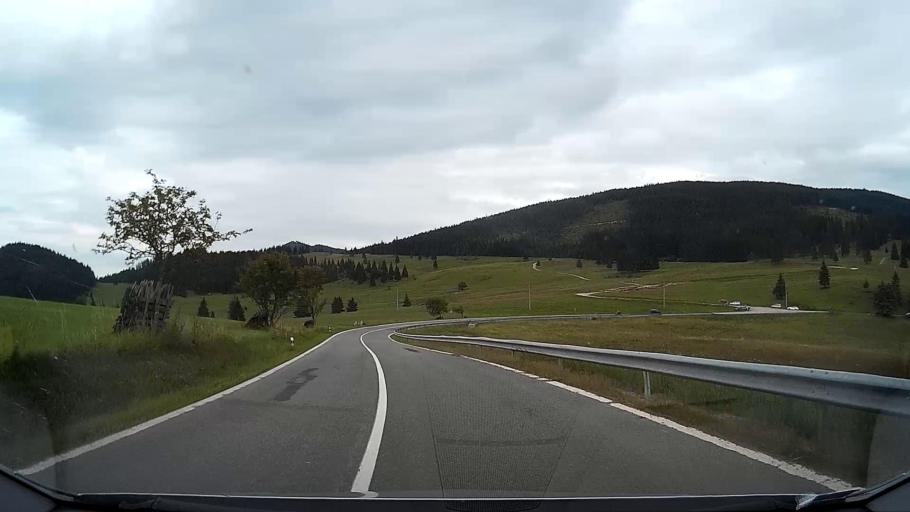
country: SK
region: Kosicky
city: Dobsina
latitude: 48.8633
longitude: 20.2254
